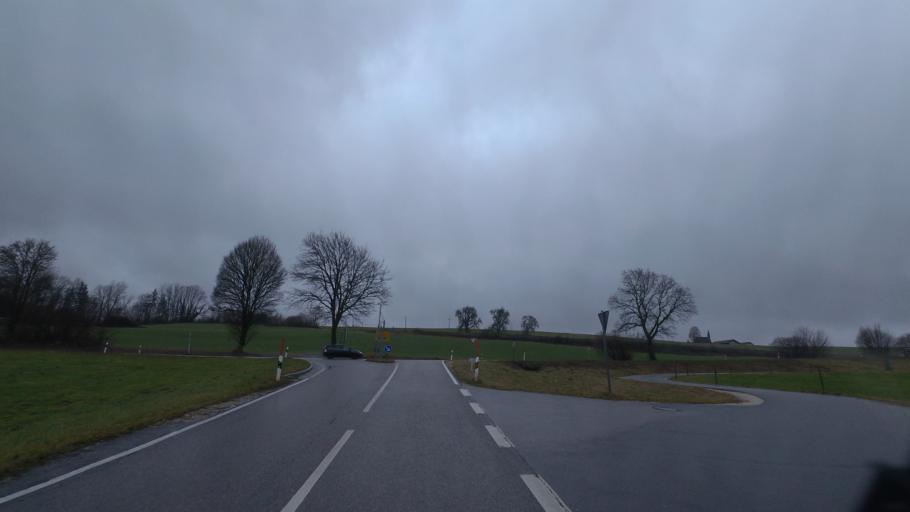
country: DE
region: Bavaria
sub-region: Upper Bavaria
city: Sankt Leonhard am Wonneberg
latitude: 47.9195
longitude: 12.7026
